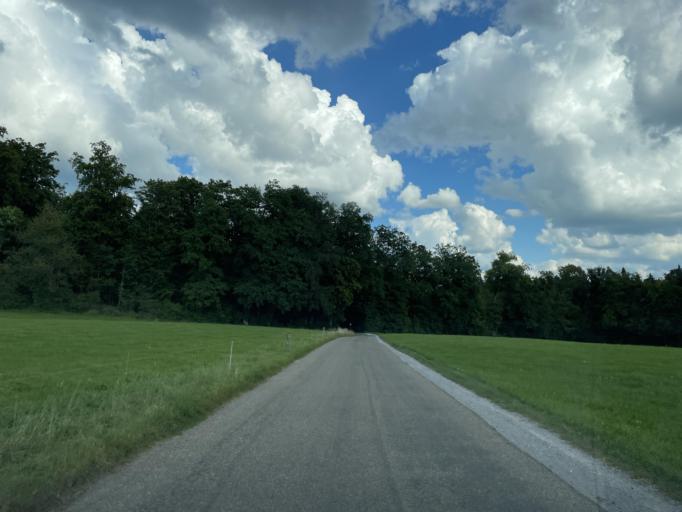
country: CH
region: Zurich
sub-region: Bezirk Winterthur
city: Mattenbach (Kreis 7)
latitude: 47.4751
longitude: 8.7462
